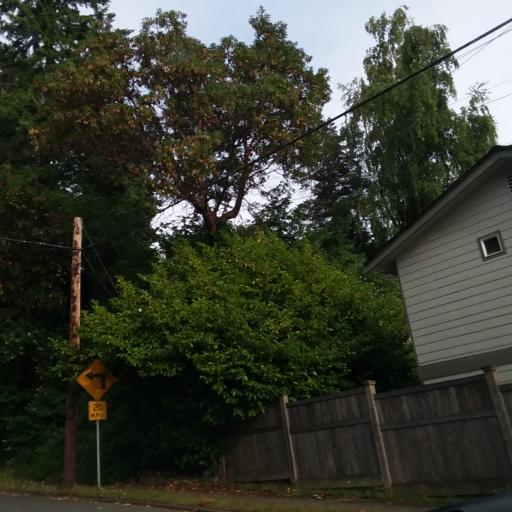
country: US
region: Washington
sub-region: King County
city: Seattle
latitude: 47.5792
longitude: -122.3961
